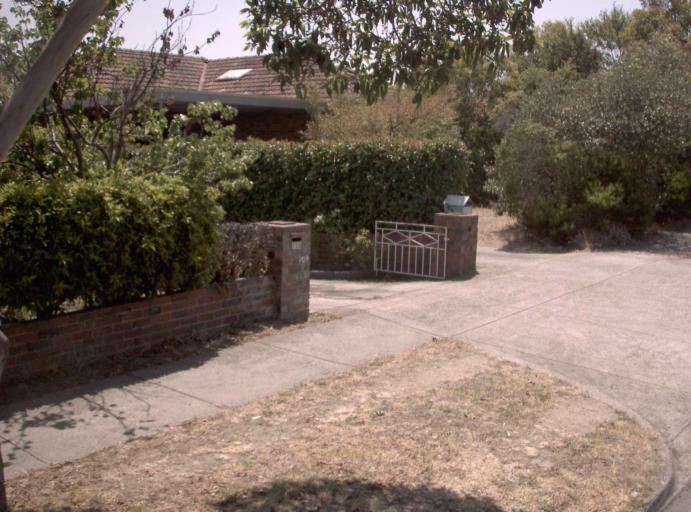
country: AU
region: Victoria
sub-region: Manningham
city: Bulleen
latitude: -37.7748
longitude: 145.0923
